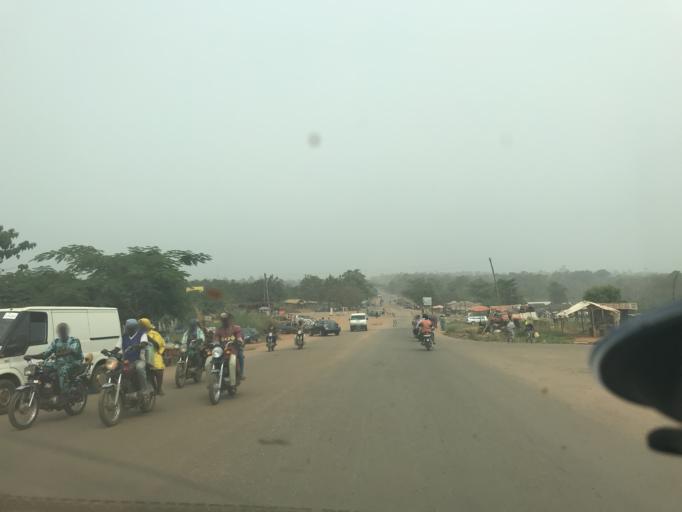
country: NG
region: Ogun
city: Ilaro
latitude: 6.8962
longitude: 3.0215
